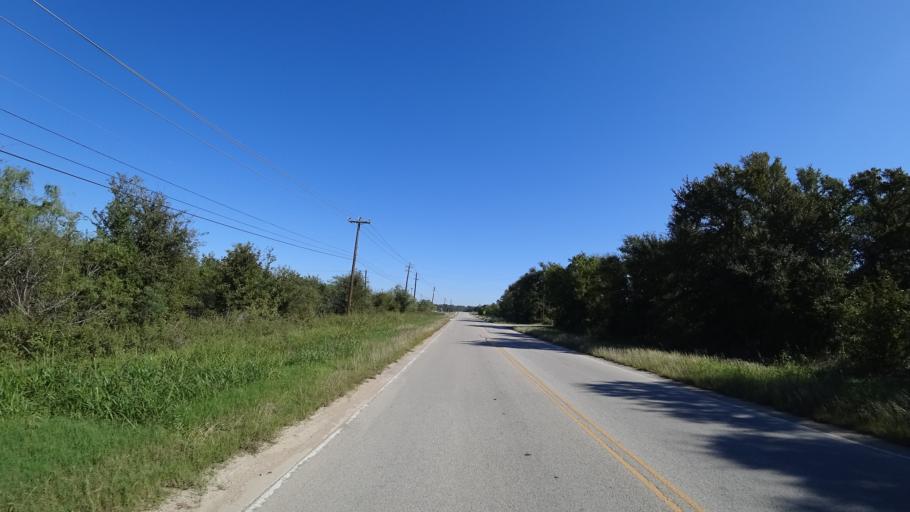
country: US
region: Texas
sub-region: Travis County
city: Hornsby Bend
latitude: 30.2547
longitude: -97.5936
